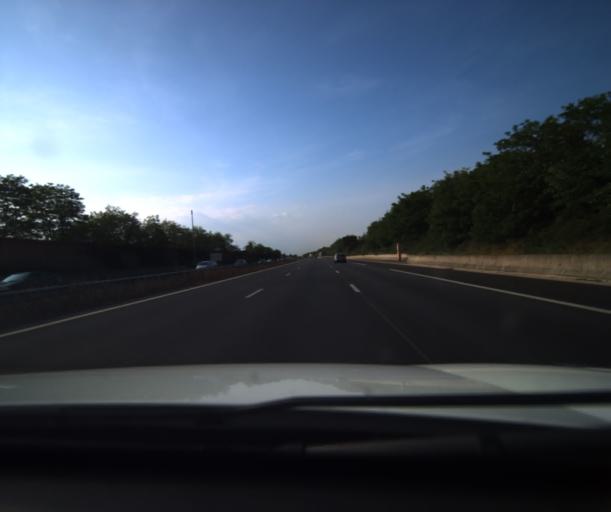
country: FR
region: Midi-Pyrenees
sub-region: Departement de la Haute-Garonne
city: Saint-Alban
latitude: 43.6884
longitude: 1.4119
